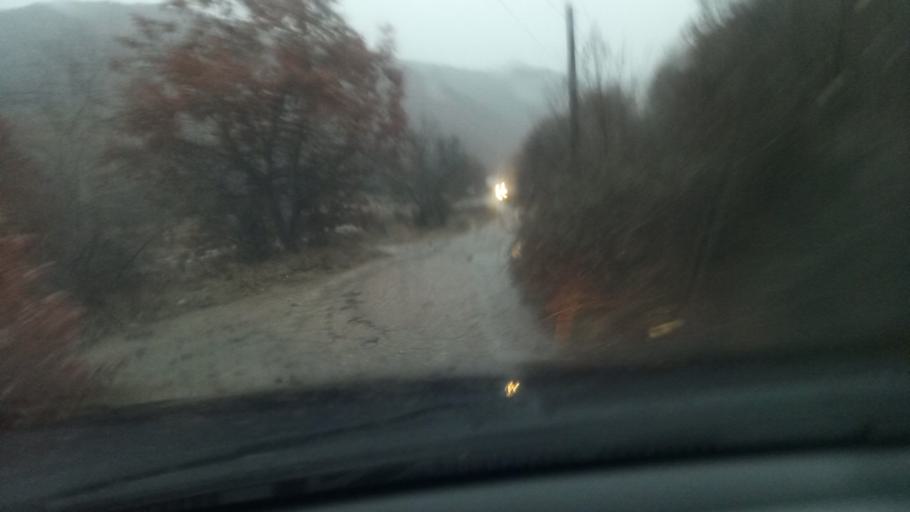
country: MK
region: Vinica
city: Blatec
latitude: 41.8405
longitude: 22.6141
